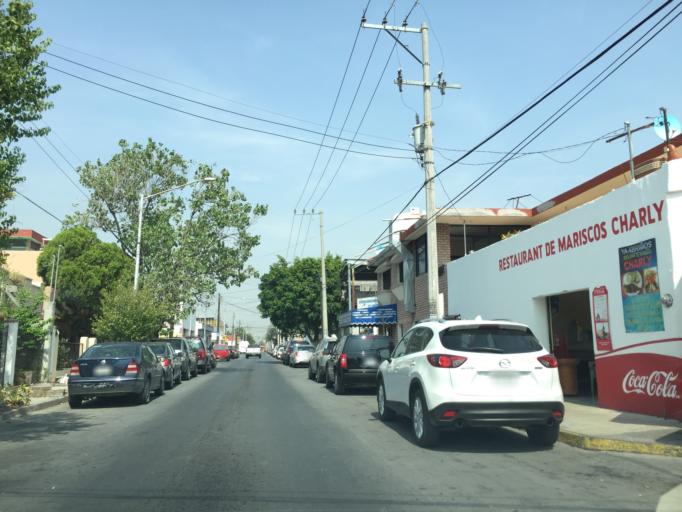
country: MX
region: Nuevo Leon
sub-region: Monterrey
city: Monterrey
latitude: 25.6616
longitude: -100.3009
